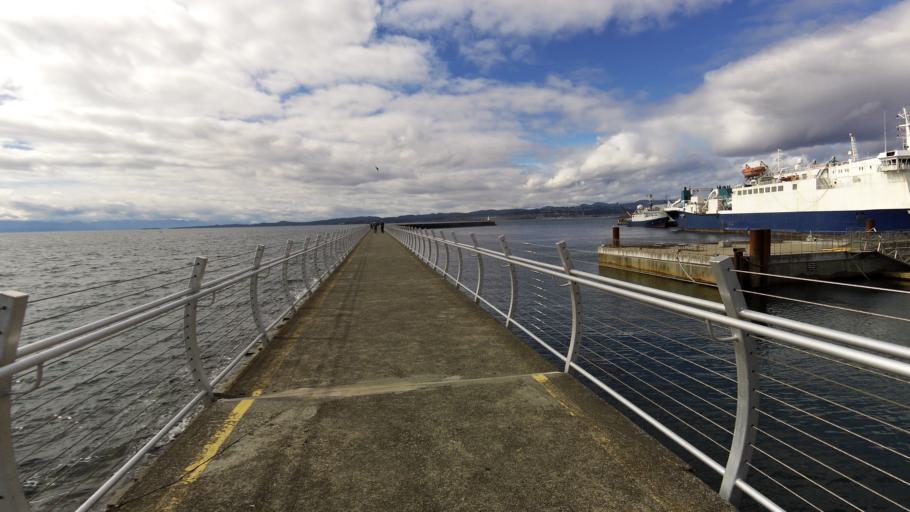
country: CA
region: British Columbia
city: Victoria
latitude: 48.4139
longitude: -123.3863
